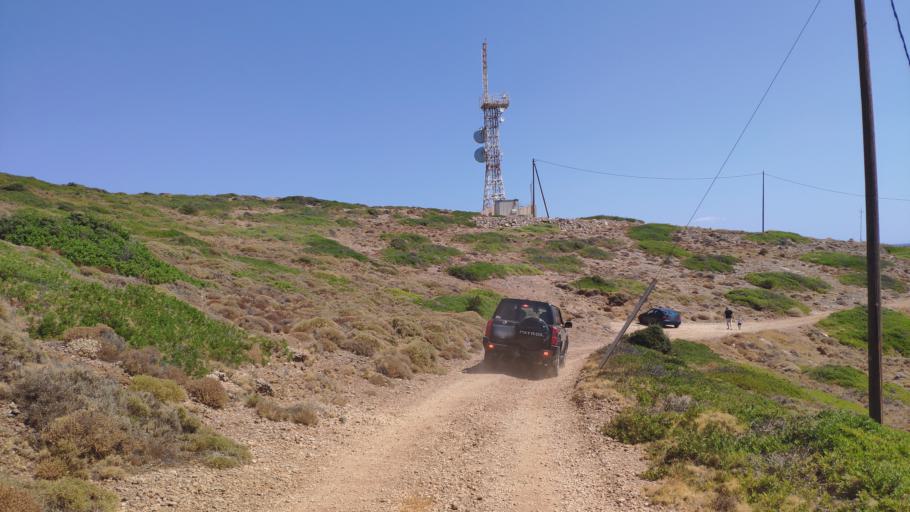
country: GR
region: Attica
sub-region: Nomarchia Anatolikis Attikis
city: Lavrio
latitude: 37.7439
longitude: 24.0792
